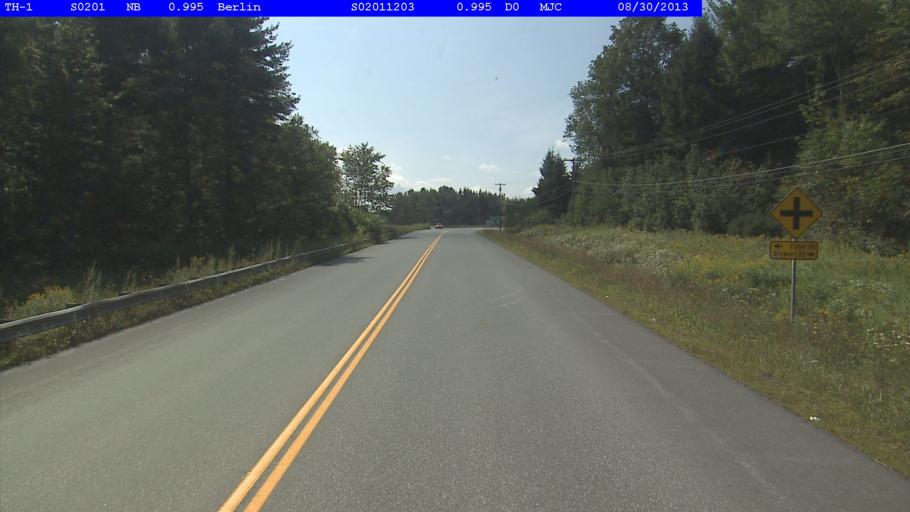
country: US
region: Vermont
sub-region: Washington County
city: Montpelier
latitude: 44.2242
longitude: -72.5665
